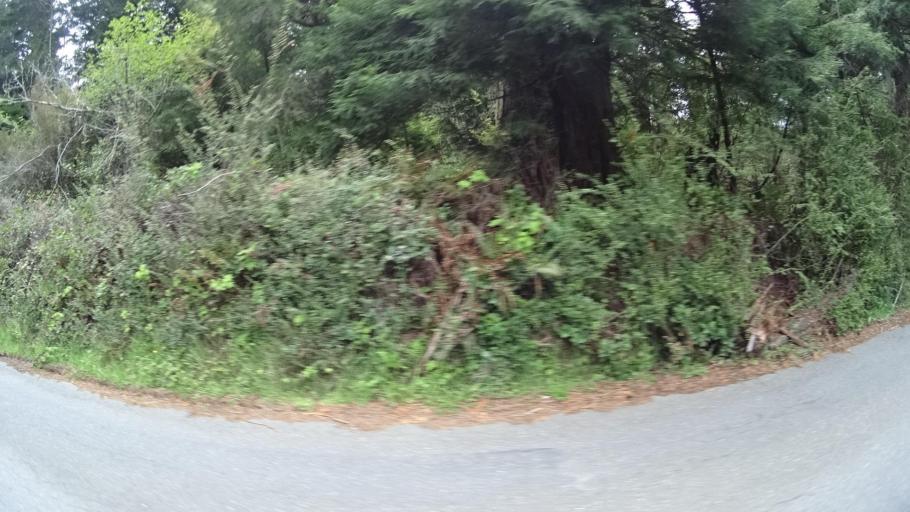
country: US
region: California
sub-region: Humboldt County
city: Bayside
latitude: 40.7969
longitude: -124.0528
